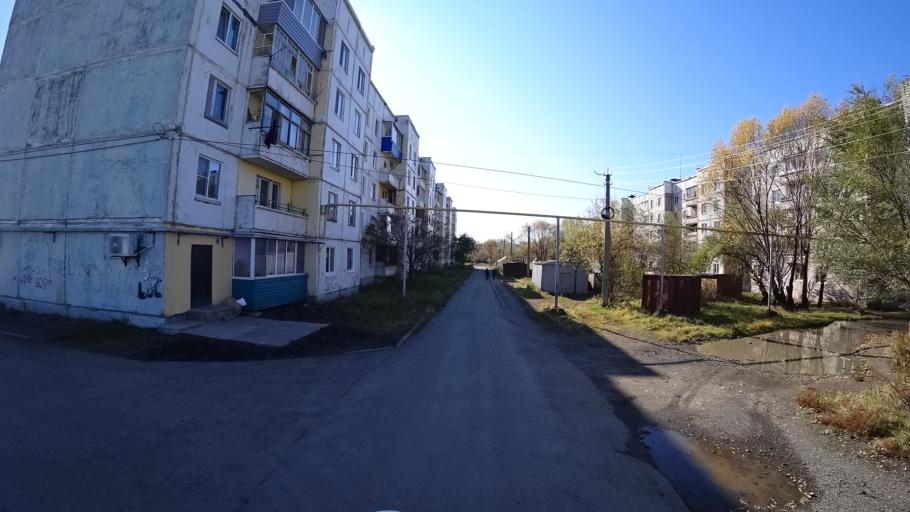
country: RU
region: Khabarovsk Krai
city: Amursk
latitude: 50.1048
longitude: 136.5168
